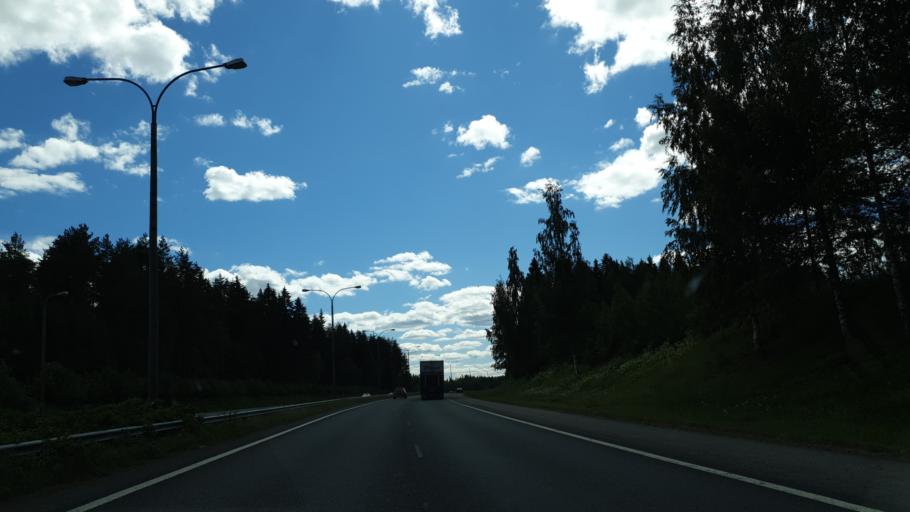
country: FI
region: Northern Savo
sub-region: Kuopio
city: Siilinjaervi
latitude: 63.0550
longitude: 27.6709
